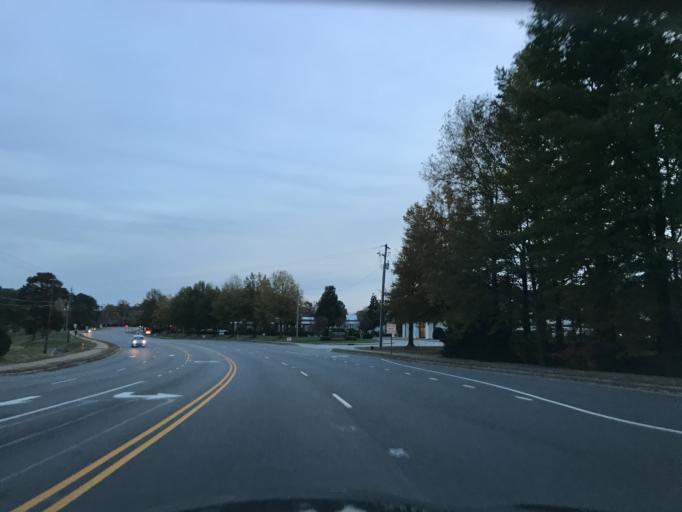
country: US
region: North Carolina
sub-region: Wake County
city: West Raleigh
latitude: 35.8614
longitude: -78.6192
